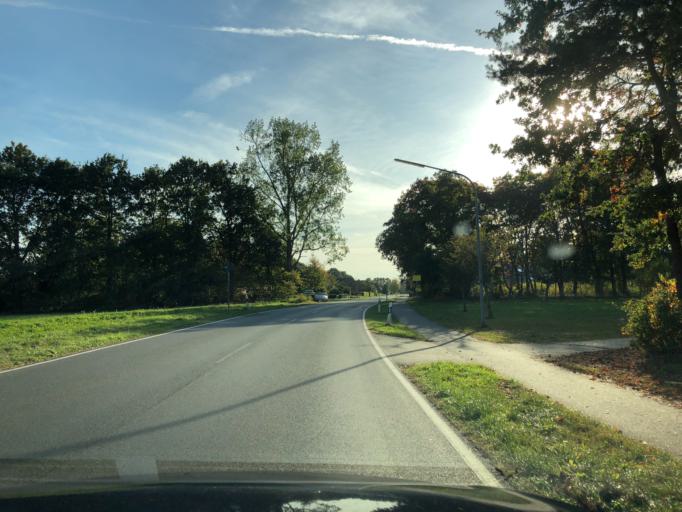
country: DE
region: Lower Saxony
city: Papenburg
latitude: 53.0450
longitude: 7.4033
